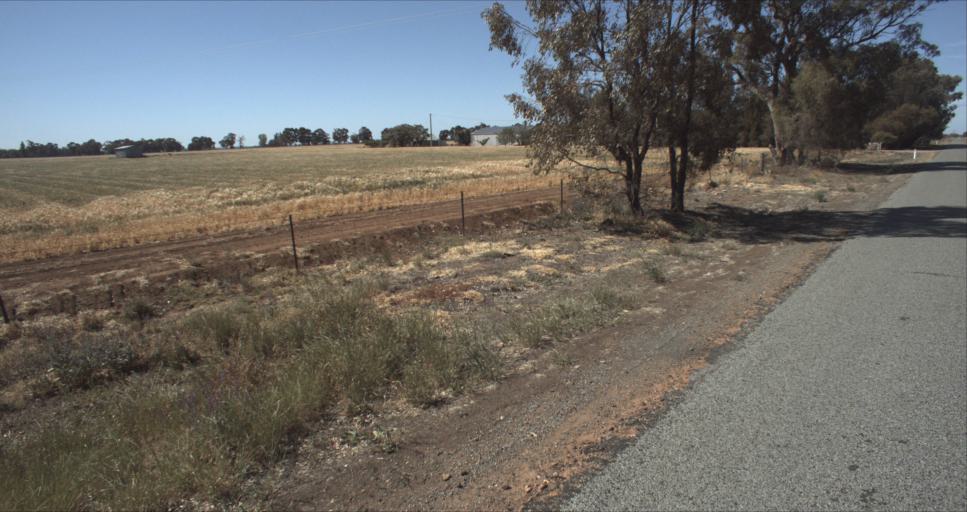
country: AU
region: New South Wales
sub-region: Leeton
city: Leeton
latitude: -34.5434
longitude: 146.3160
